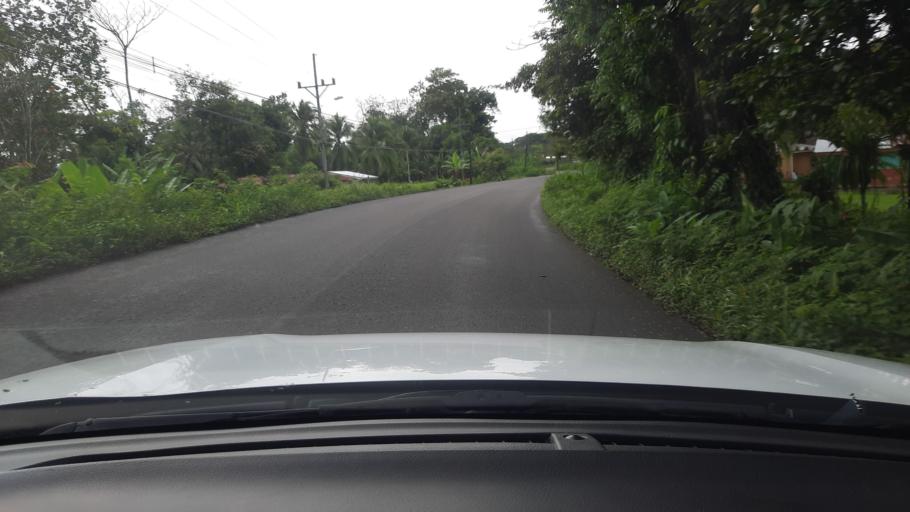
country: CR
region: Alajuela
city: San Jose
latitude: 10.9531
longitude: -85.1266
